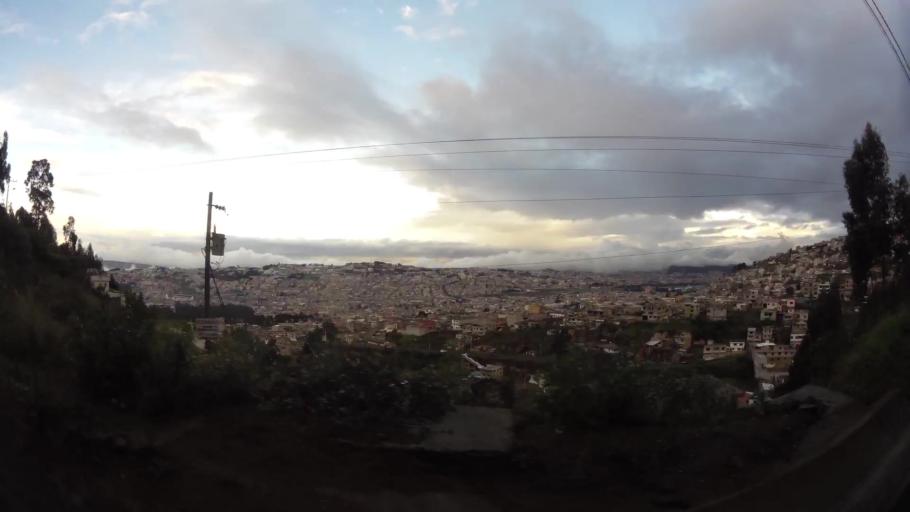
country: EC
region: Pichincha
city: Quito
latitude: -0.1161
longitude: -78.5140
